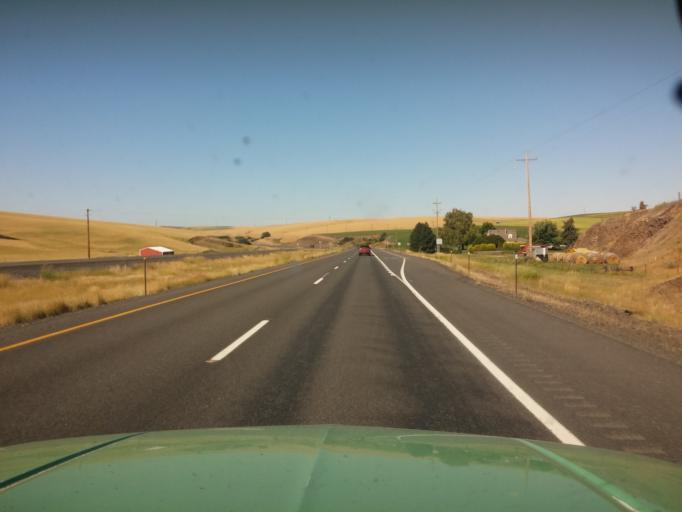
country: US
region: Idaho
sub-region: Nez Perce County
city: Lewiston
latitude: 46.4904
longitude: -117.0225
